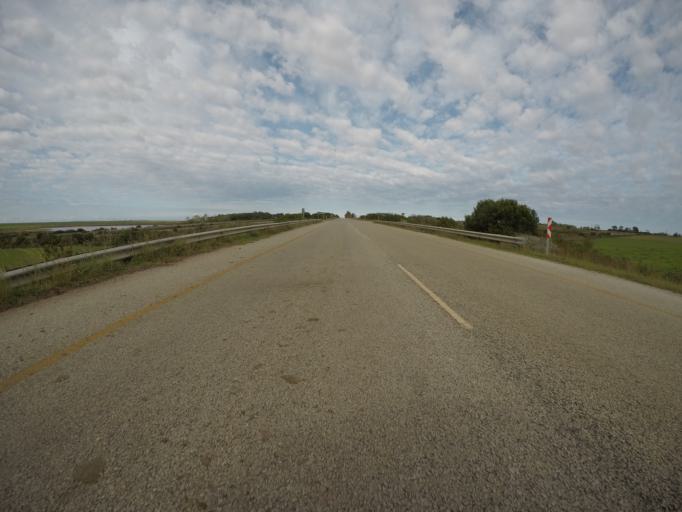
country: ZA
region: Eastern Cape
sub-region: Cacadu District Municipality
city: Kareedouw
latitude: -34.0491
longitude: 24.4566
